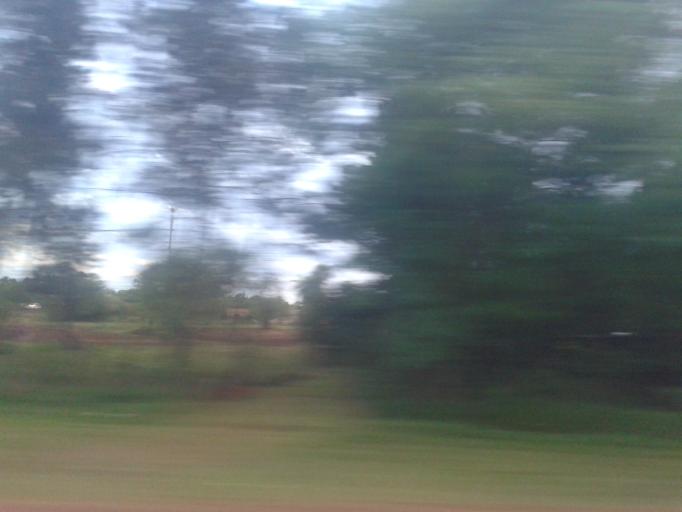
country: AR
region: Misiones
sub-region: Departamento de Candelaria
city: Candelaria
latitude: -27.4715
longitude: -55.7392
